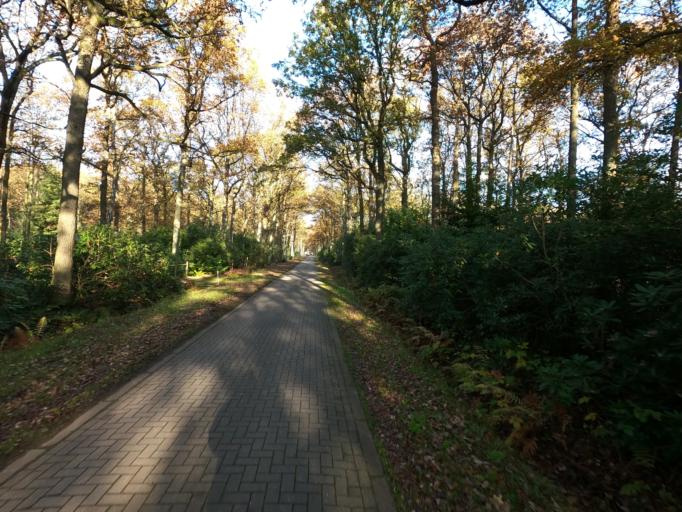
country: BE
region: Flanders
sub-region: Provincie Antwerpen
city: Brasschaat
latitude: 51.3420
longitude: 4.5274
